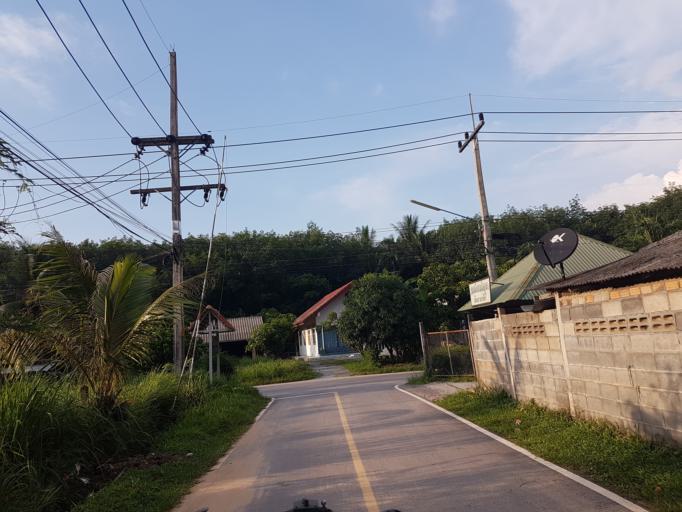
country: TH
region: Pattani
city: Khok Pho
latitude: 6.6762
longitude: 101.0943
